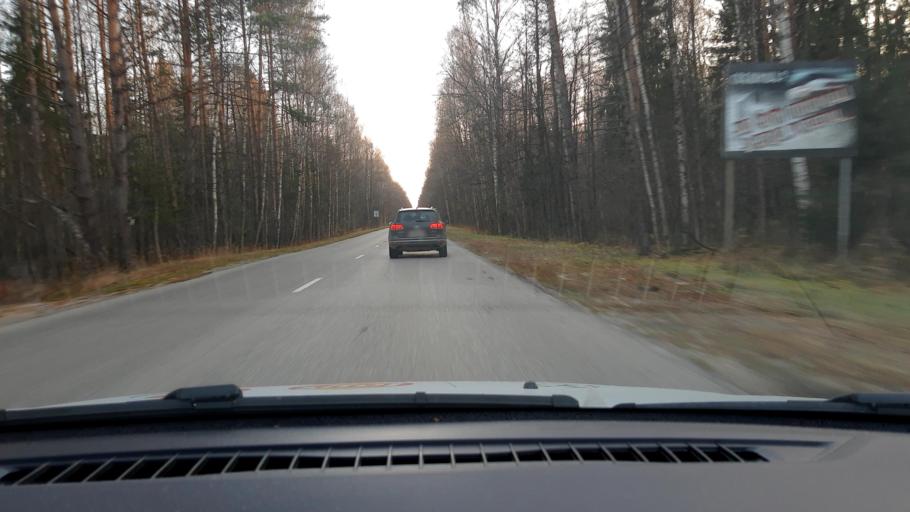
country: RU
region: Nizjnij Novgorod
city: Volodarsk
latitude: 56.2772
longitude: 43.1665
